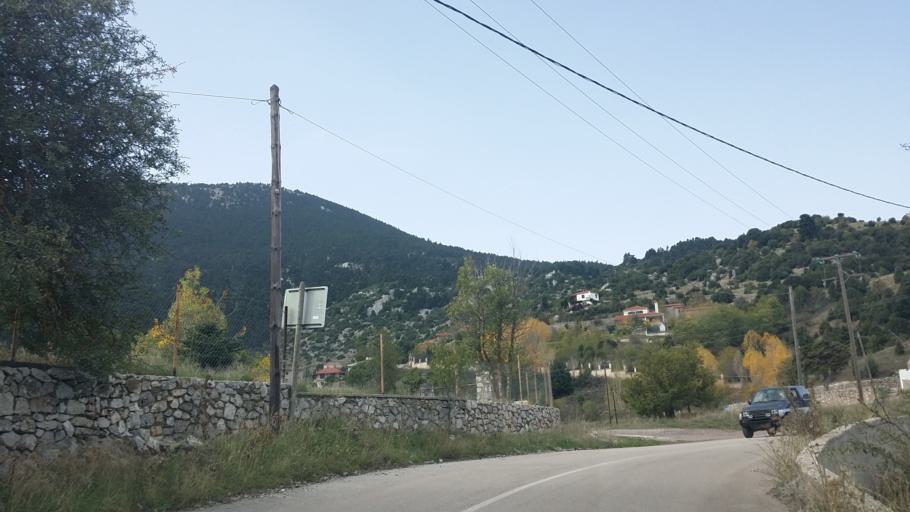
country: GR
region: Central Greece
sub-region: Nomos Voiotias
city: Kyriaki
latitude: 38.3686
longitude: 22.8445
